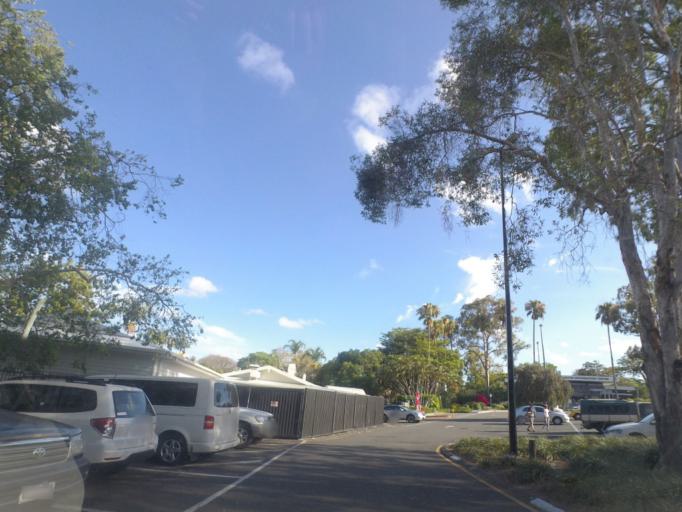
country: AU
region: Queensland
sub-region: Brisbane
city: Toowong
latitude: -27.4752
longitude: 152.9775
